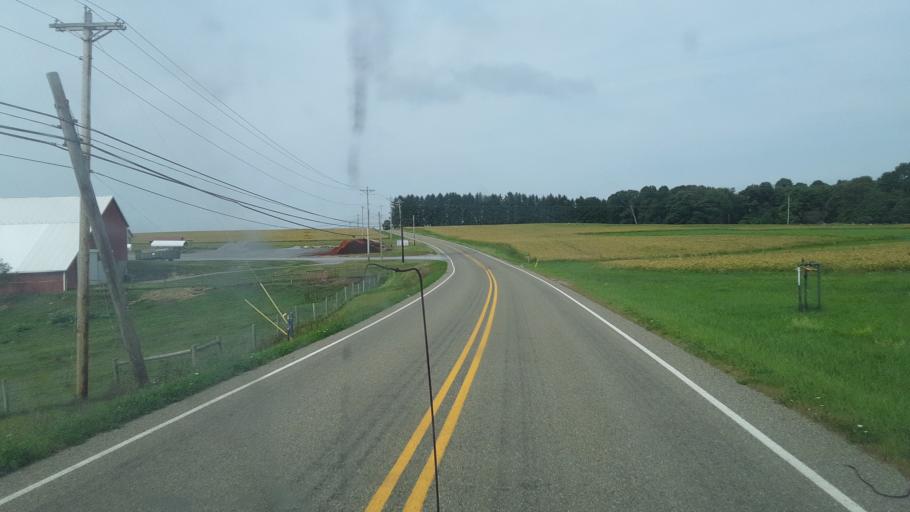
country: US
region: Pennsylvania
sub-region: Jefferson County
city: Punxsutawney
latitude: 40.9626
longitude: -79.0852
